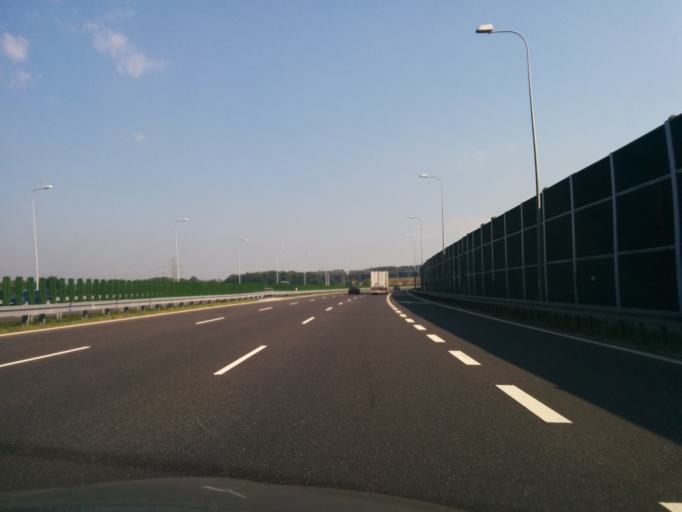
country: PL
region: Silesian Voivodeship
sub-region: Gliwice
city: Gliwice
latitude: 50.3116
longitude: 18.7261
